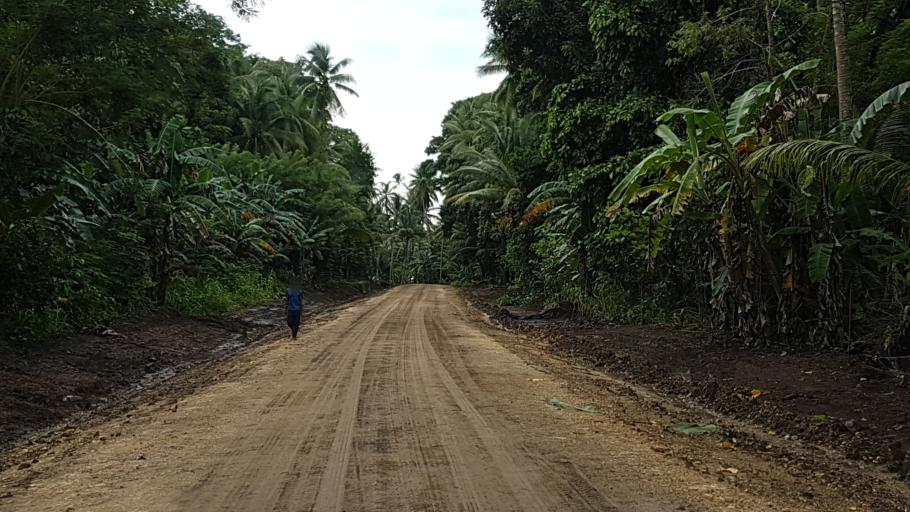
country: PG
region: Milne Bay
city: Alotau
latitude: -10.2953
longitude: 150.7500
